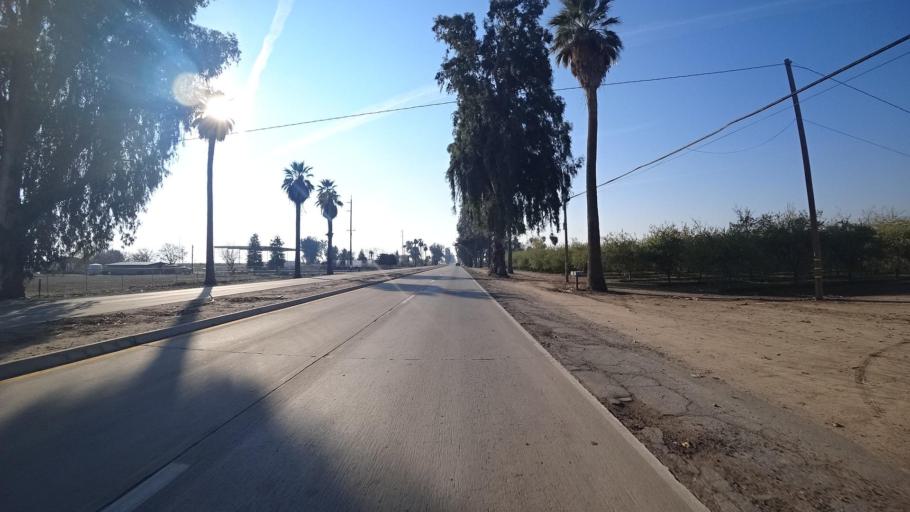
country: US
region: California
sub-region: Kern County
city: Greenfield
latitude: 35.2342
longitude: -119.0032
